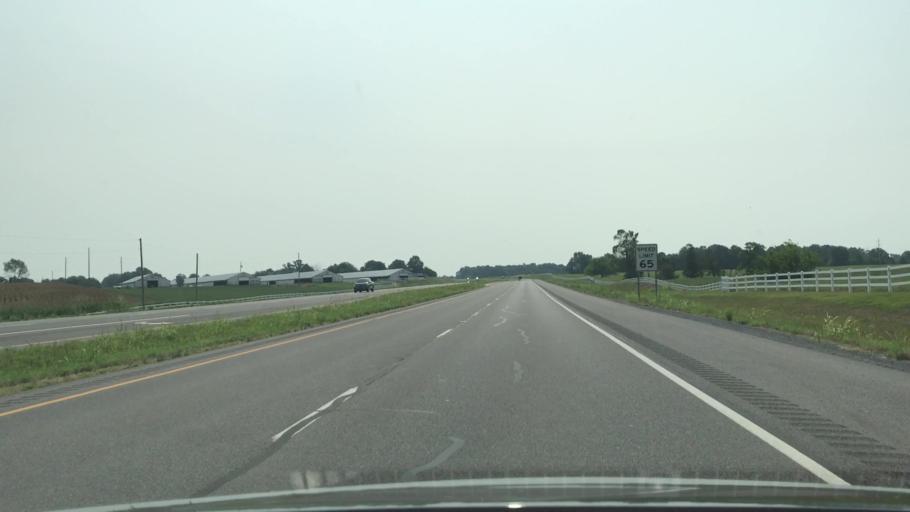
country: US
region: Kentucky
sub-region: Graves County
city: Mayfield
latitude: 36.6813
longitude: -88.5327
